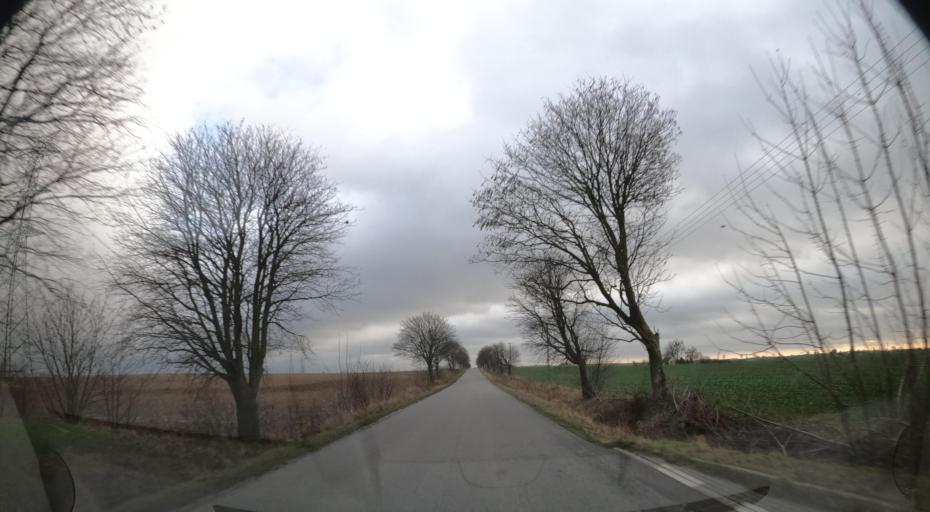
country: PL
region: Kujawsko-Pomorskie
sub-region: Powiat nakielski
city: Sadki
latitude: 53.1771
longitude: 17.4165
